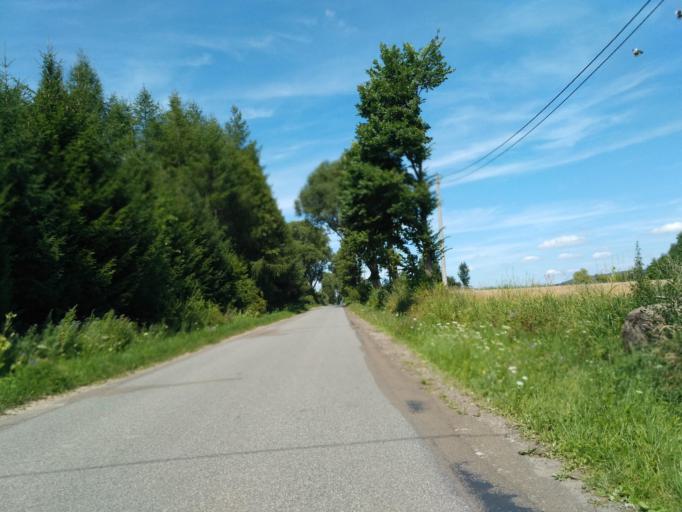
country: PL
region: Subcarpathian Voivodeship
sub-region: Powiat sanocki
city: Nowosielce-Gniewosz
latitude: 49.5677
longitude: 22.1205
